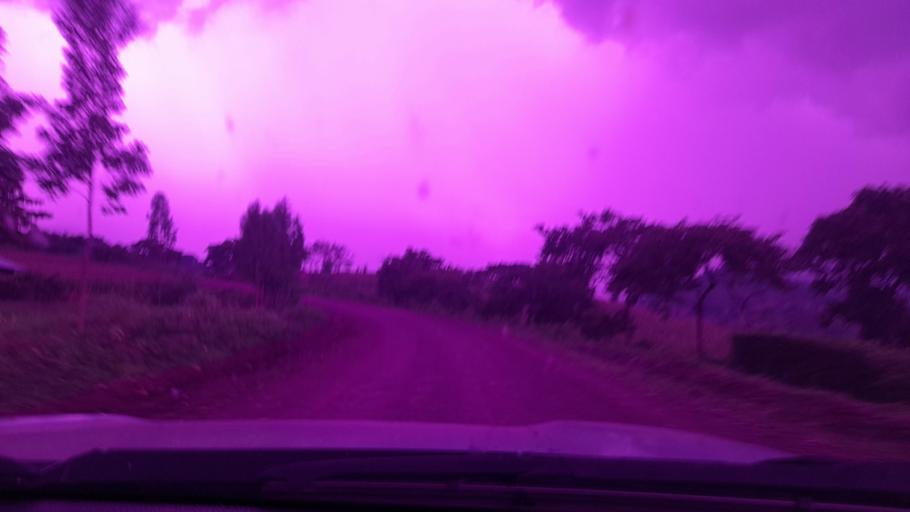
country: ET
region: Southern Nations, Nationalities, and People's Region
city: Mizan Teferi
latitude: 6.7371
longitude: 35.8654
